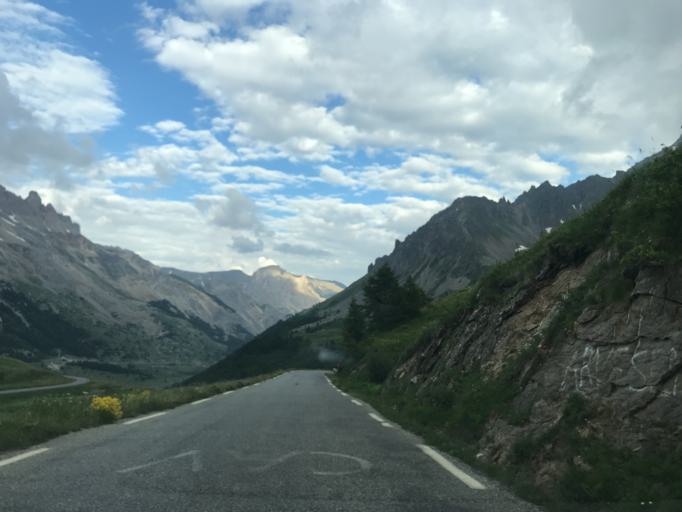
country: FR
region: Provence-Alpes-Cote d'Azur
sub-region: Departement des Hautes-Alpes
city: Le Monetier-les-Bains
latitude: 45.0385
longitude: 6.4016
